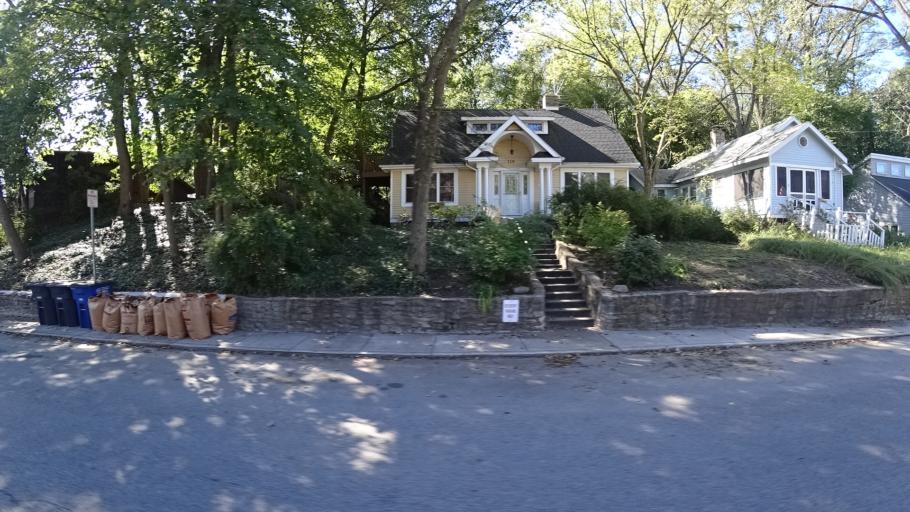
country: US
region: Indiana
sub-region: LaPorte County
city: Michigan City
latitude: 41.7278
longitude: -86.8910
